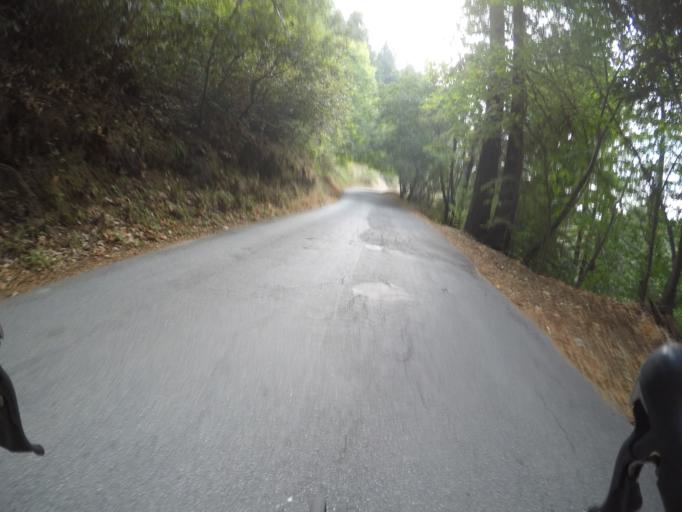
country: US
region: California
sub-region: Santa Cruz County
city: Scotts Valley
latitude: 37.0606
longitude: -122.0187
